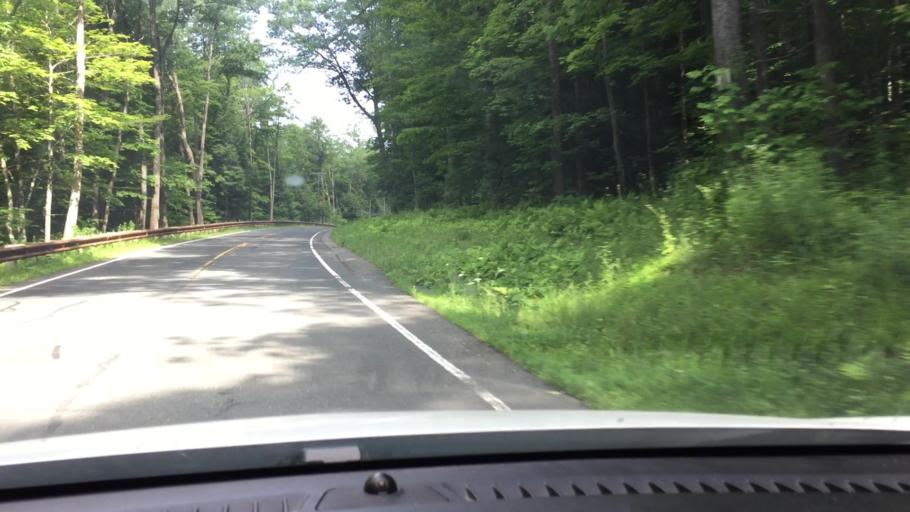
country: US
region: Massachusetts
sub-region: Berkshire County
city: Otis
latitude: 42.2074
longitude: -73.1706
